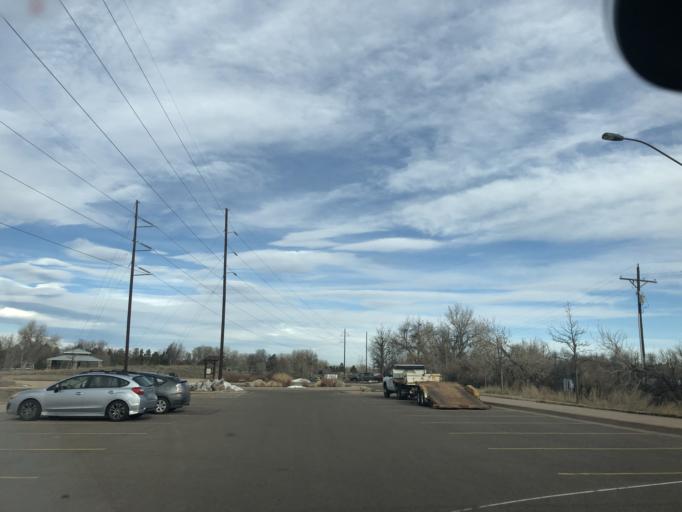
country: US
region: Colorado
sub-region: Arapahoe County
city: Columbine Valley
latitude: 39.5950
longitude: -105.0261
